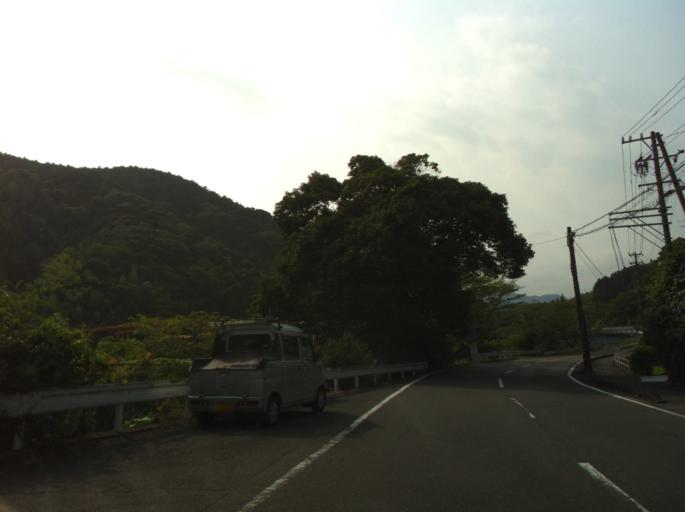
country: JP
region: Shizuoka
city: Fujieda
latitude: 34.9293
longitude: 138.2708
